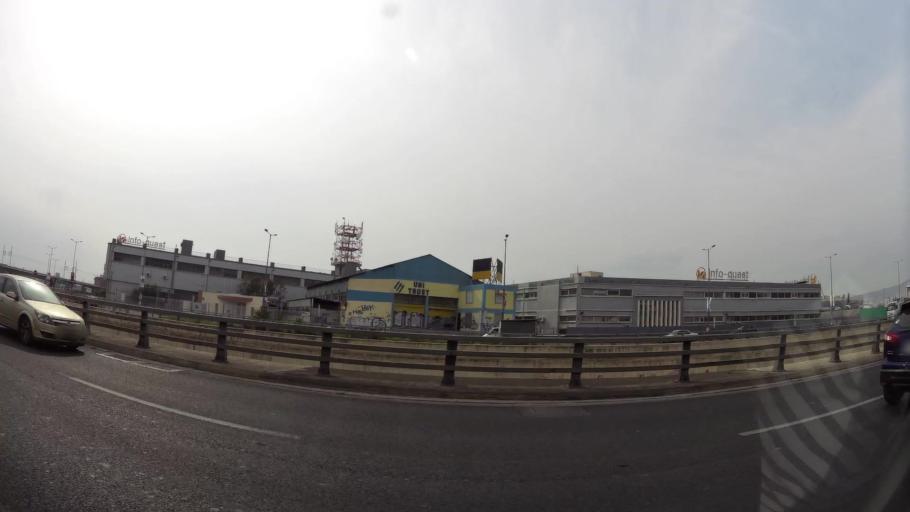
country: GR
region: Attica
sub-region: Nomarchia Athinas
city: Tavros
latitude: 37.9675
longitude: 23.6782
